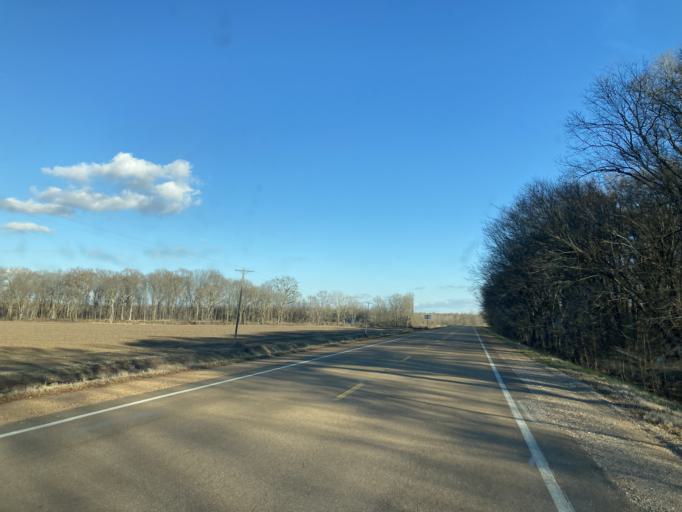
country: US
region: Mississippi
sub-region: Yazoo County
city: Yazoo City
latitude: 32.9251
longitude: -90.5741
